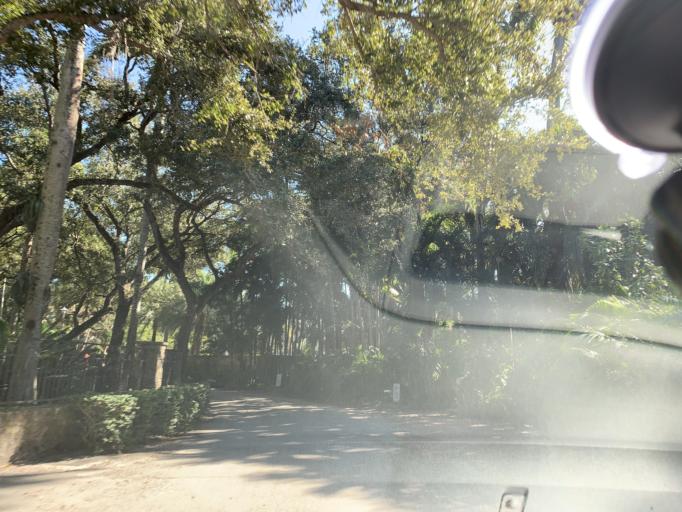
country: US
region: Florida
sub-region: Miami-Dade County
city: Coconut Grove
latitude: 25.7187
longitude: -80.2552
